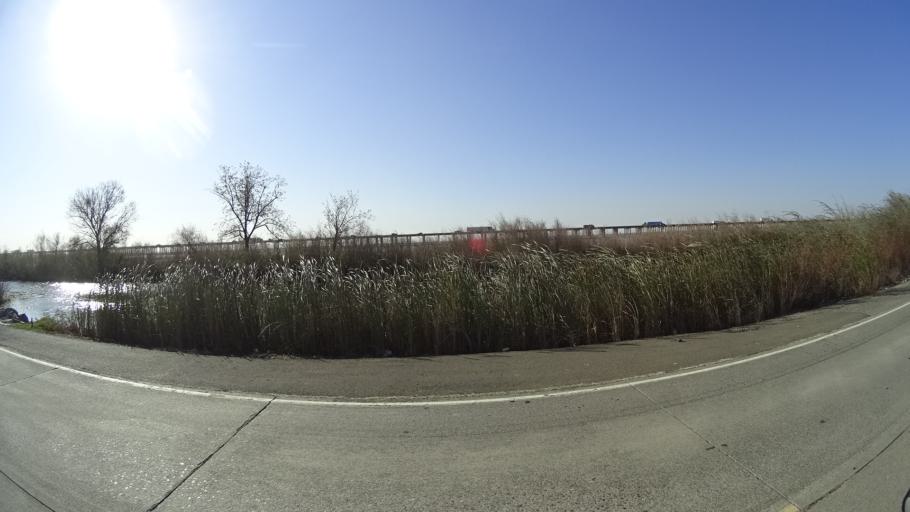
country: US
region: California
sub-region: Yolo County
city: Woodland
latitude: 38.6767
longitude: -121.6637
